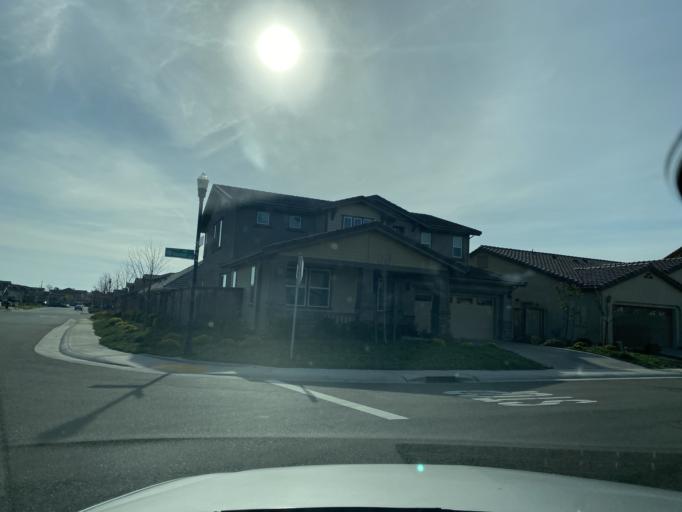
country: US
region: California
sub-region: Sacramento County
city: Elk Grove
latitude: 38.3986
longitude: -121.3848
